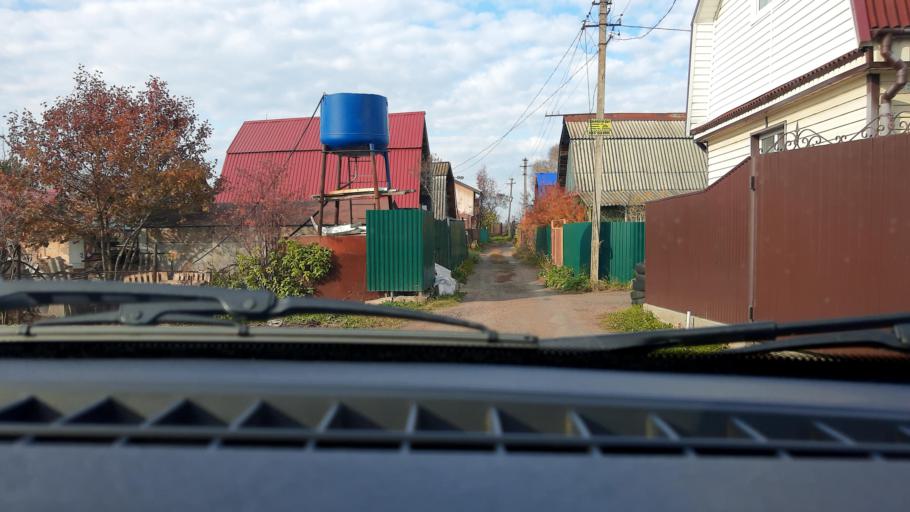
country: RU
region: Bashkortostan
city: Ufa
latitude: 54.6004
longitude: 55.8958
